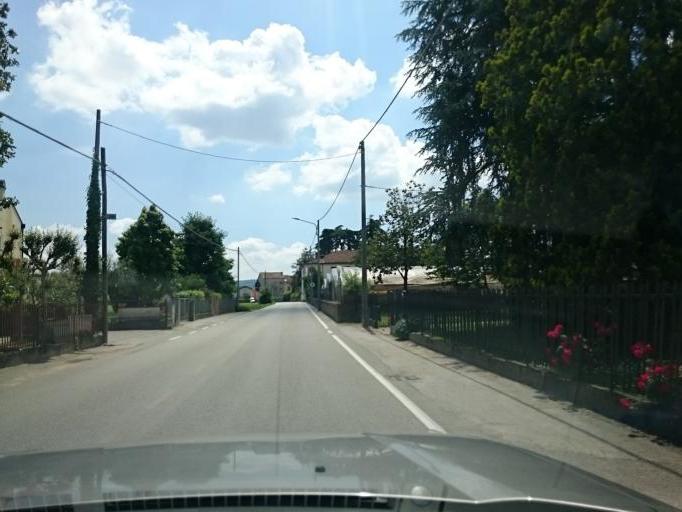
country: IT
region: Veneto
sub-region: Provincia di Vicenza
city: Vicenza
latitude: 45.5328
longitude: 11.5705
